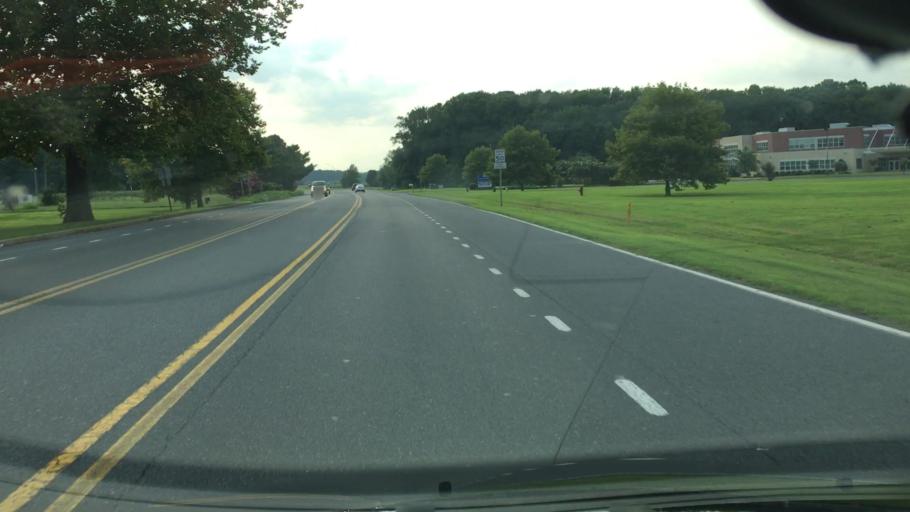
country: US
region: Maryland
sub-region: Worcester County
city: Ocean Pines
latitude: 38.3877
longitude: -75.1873
